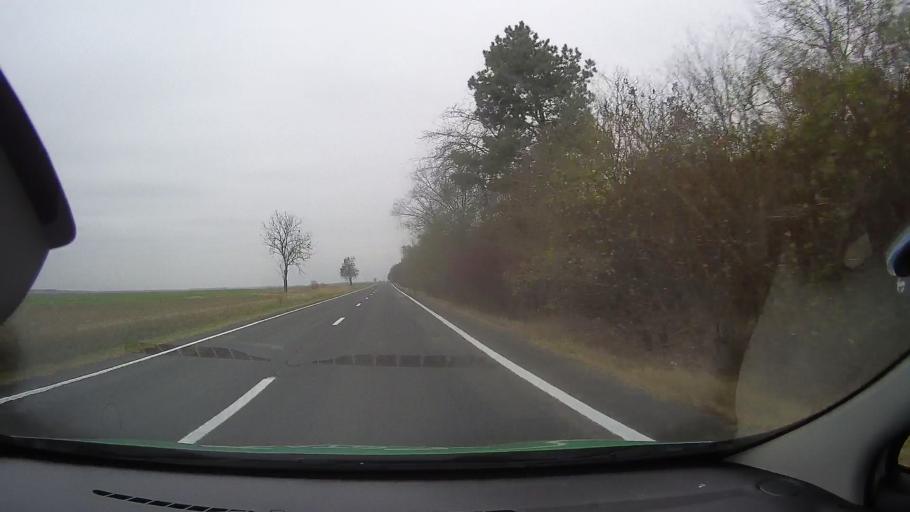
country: RO
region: Ialomita
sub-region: Comuna Mihail Kogalniceanu
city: Mihail Kogalniceanu
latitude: 44.6646
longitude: 27.7422
